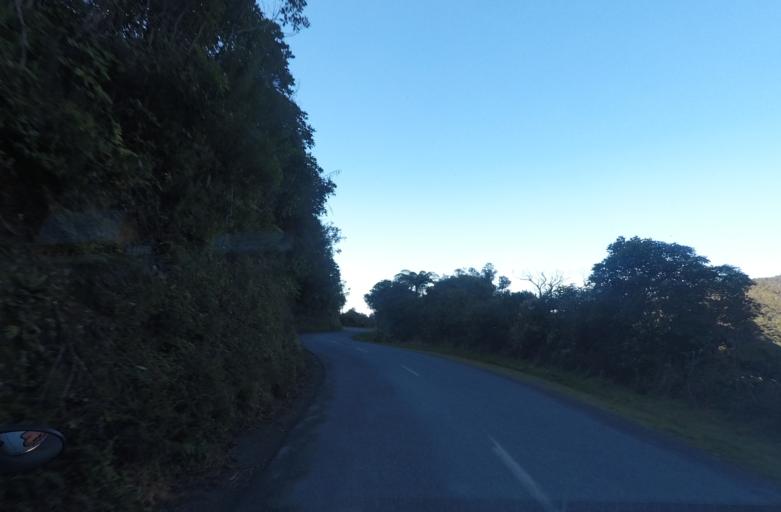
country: NZ
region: Marlborough
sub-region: Marlborough District
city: Picton
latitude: -41.2718
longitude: 173.9577
